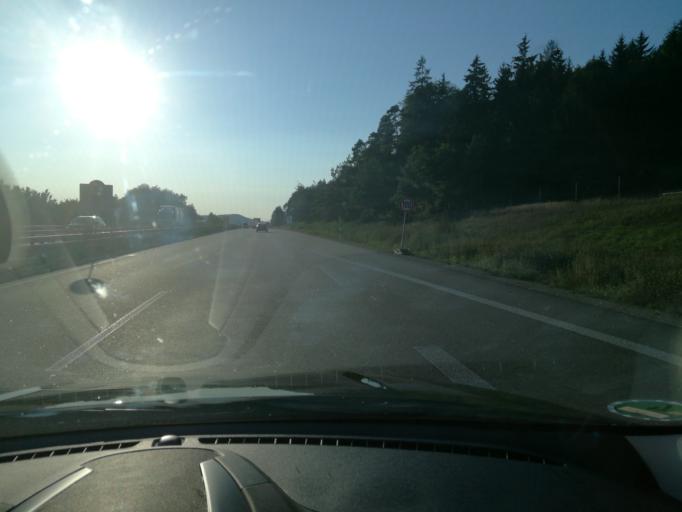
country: DE
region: Bavaria
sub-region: Upper Palatinate
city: Parsberg
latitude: 49.1796
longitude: 11.7256
